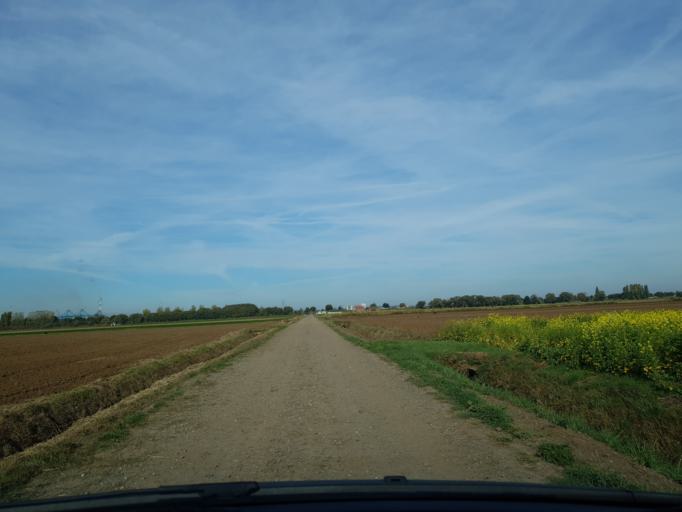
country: BE
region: Flanders
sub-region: Provincie Antwerpen
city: Stabroek
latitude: 51.3103
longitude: 4.3702
